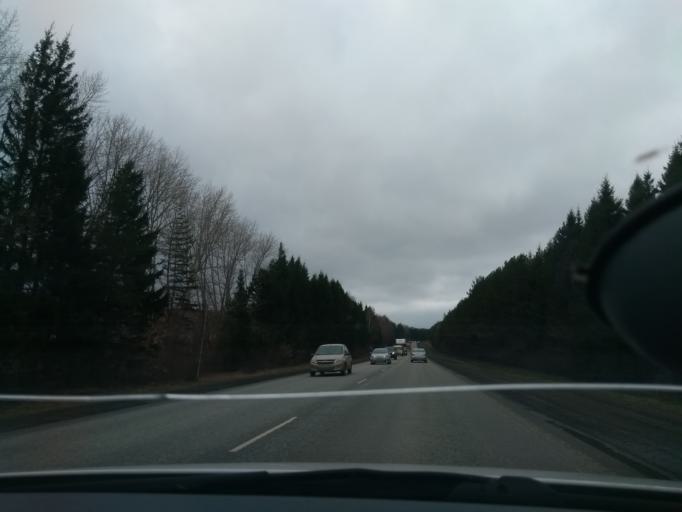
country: RU
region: Perm
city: Kungur
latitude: 57.4524
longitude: 56.7917
